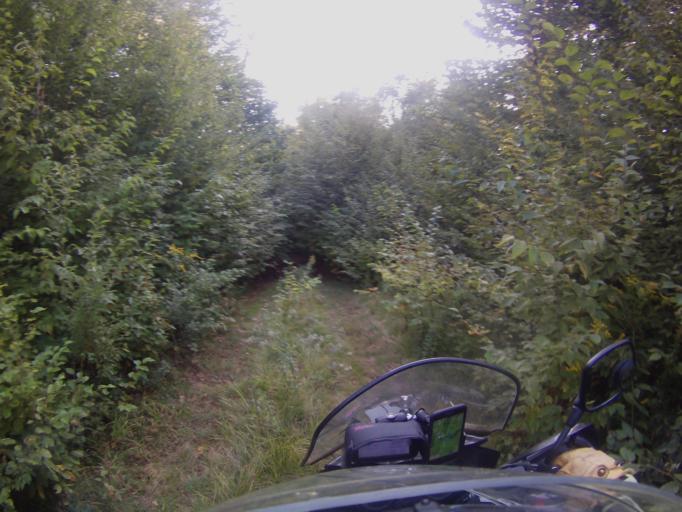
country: US
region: Vermont
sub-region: Addison County
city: Bristol
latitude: 44.0147
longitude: -72.9936
